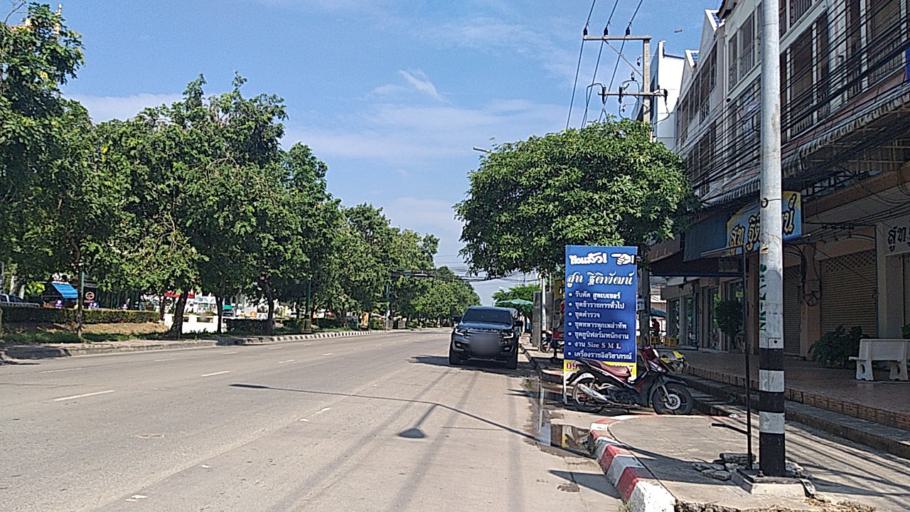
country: TH
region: Suphan Buri
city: Suphan Buri
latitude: 14.4726
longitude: 100.1249
